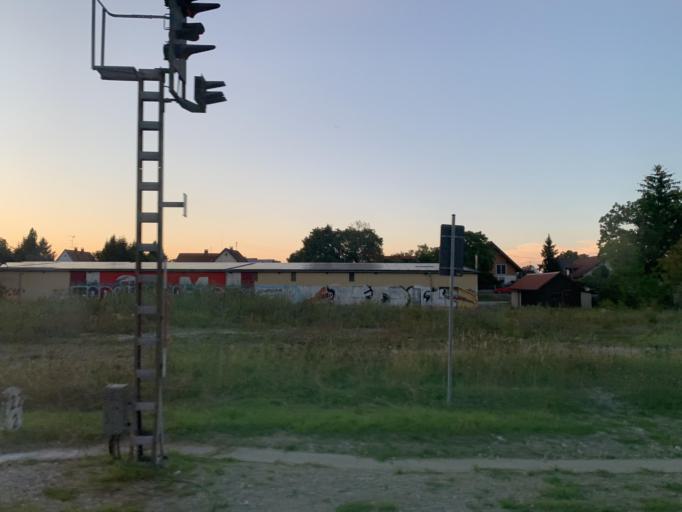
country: DE
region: Bavaria
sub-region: Upper Bavaria
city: Kaufering
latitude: 48.0801
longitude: 10.8499
